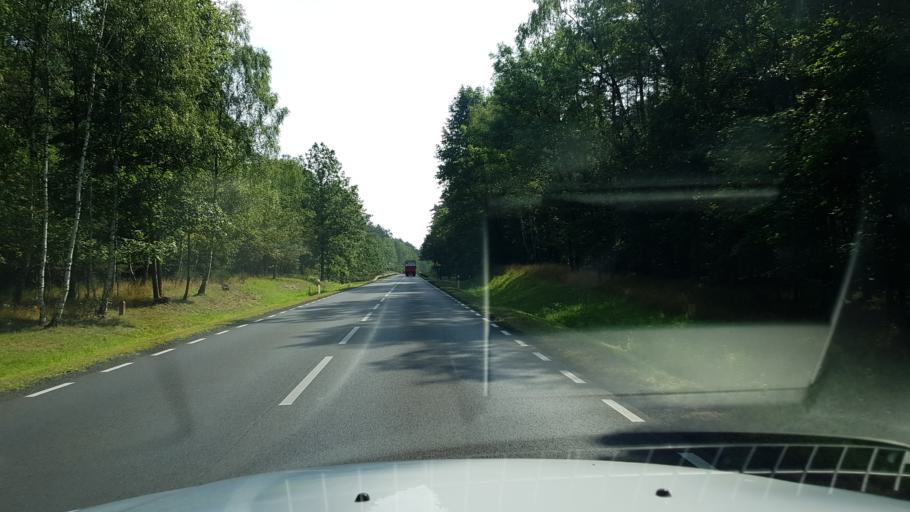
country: PL
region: West Pomeranian Voivodeship
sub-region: Powiat walecki
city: Miroslawiec
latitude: 53.3502
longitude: 16.1382
